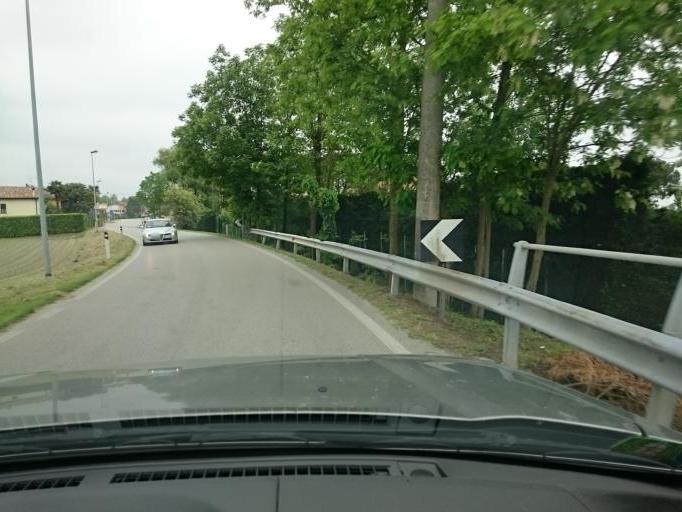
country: IT
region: Veneto
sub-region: Provincia di Padova
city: Correzzola
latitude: 45.2341
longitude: 12.0605
